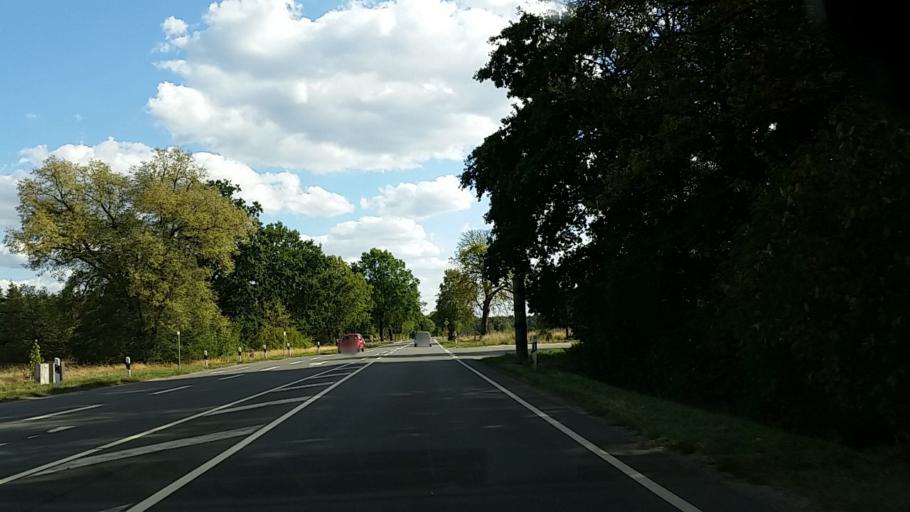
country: DE
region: Lower Saxony
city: Wagenhoff
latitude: 52.5546
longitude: 10.5120
